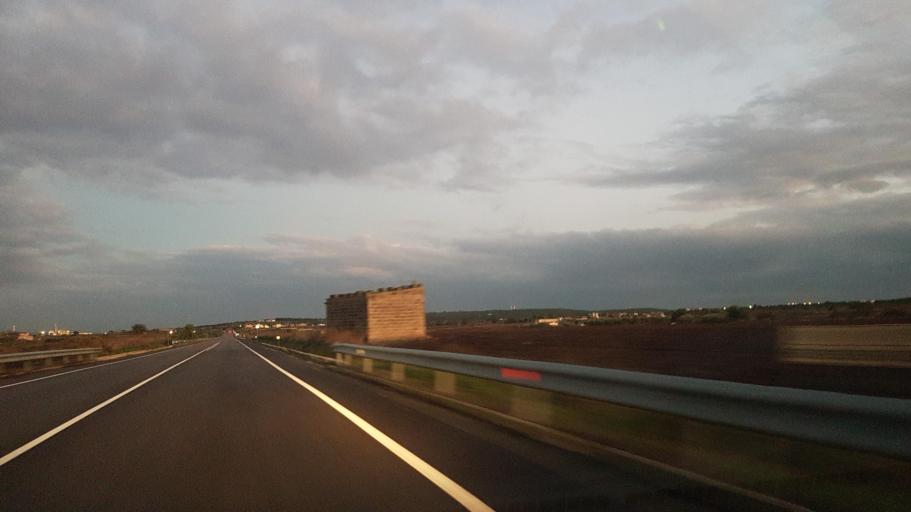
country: IT
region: Apulia
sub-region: Provincia di Taranto
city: Laterza
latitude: 40.6531
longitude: 16.7972
